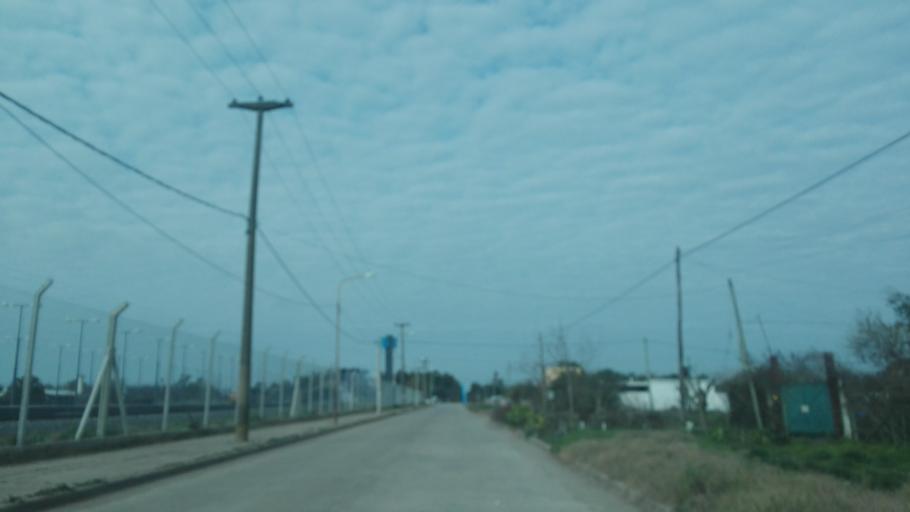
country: AR
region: Buenos Aires
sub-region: Partido de Chascomus
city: Chascomus
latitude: -35.5763
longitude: -57.9838
